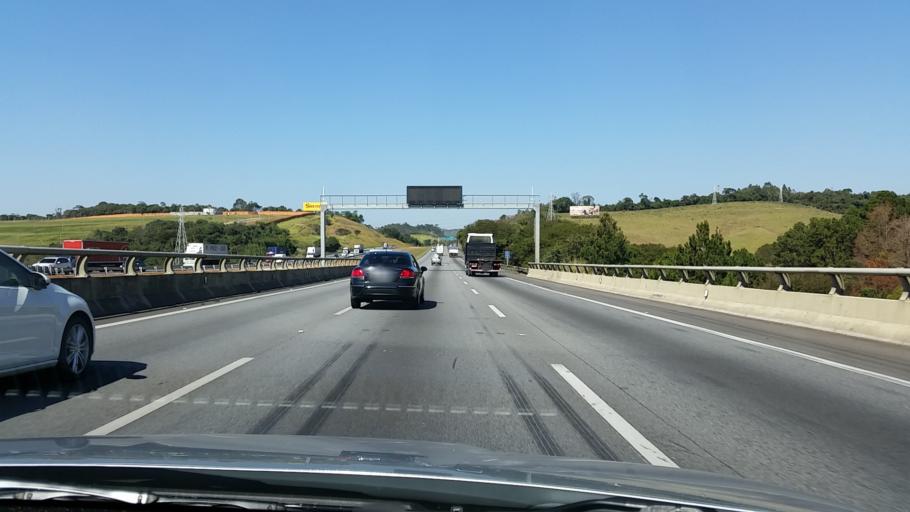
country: BR
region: Sao Paulo
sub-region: Jundiai
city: Jundiai
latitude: -23.2383
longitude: -46.8885
